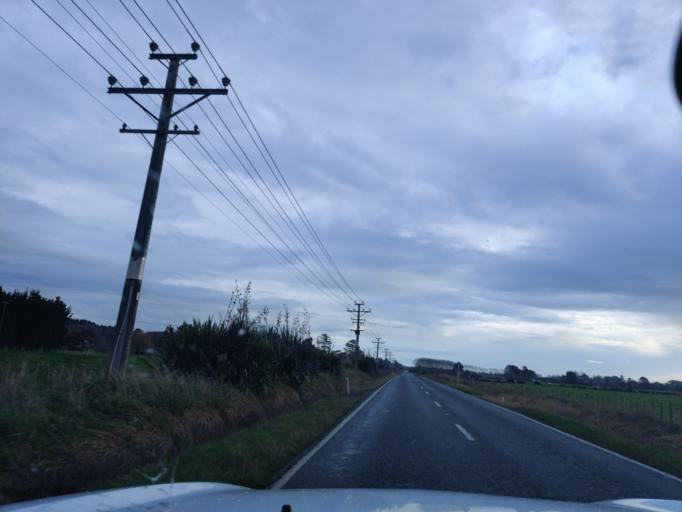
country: NZ
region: Manawatu-Wanganui
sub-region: Palmerston North City
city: Palmerston North
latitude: -40.3490
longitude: 175.7013
